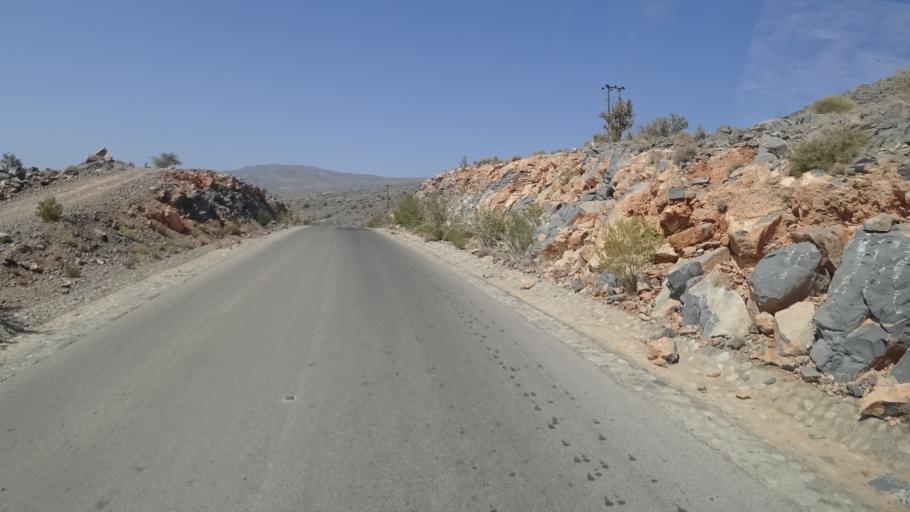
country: OM
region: Muhafazat ad Dakhiliyah
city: Bahla'
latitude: 23.1223
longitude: 57.4059
